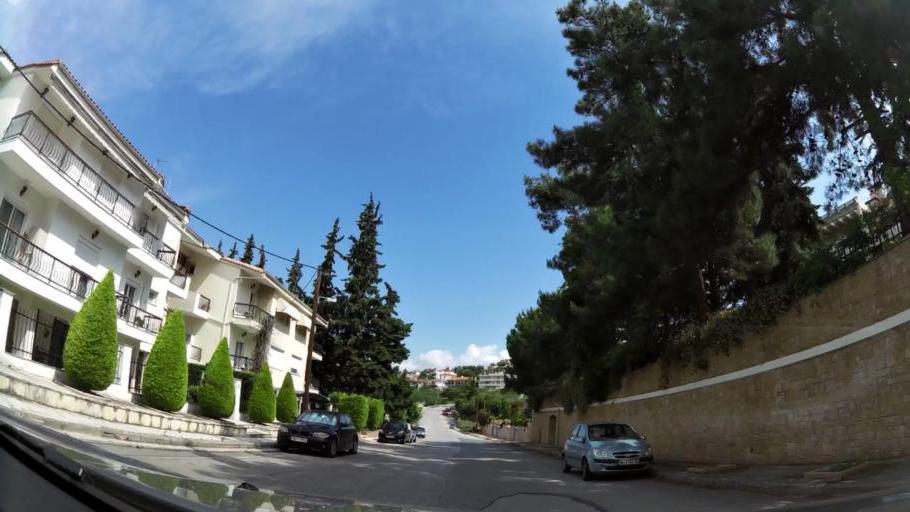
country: GR
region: Central Macedonia
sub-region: Nomos Thessalonikis
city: Panorama
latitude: 40.5837
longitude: 23.0231
